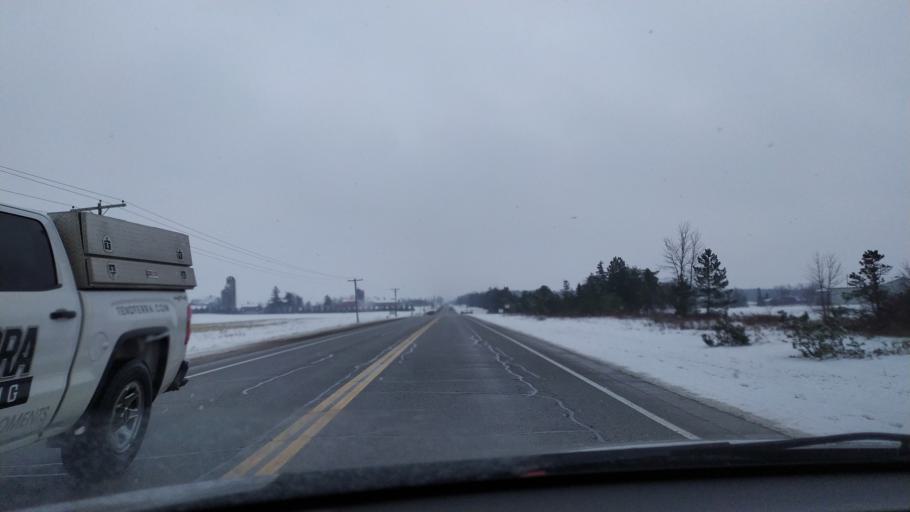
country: CA
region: Ontario
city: Waterloo
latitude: 43.6294
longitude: -80.7086
